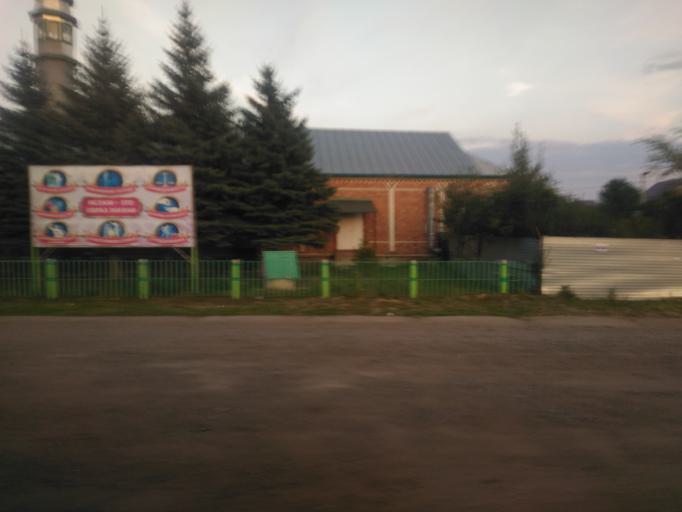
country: RU
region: Ulyanovsk
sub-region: Ulyanovskiy Rayon
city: Ulyanovsk
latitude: 54.2644
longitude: 48.2813
